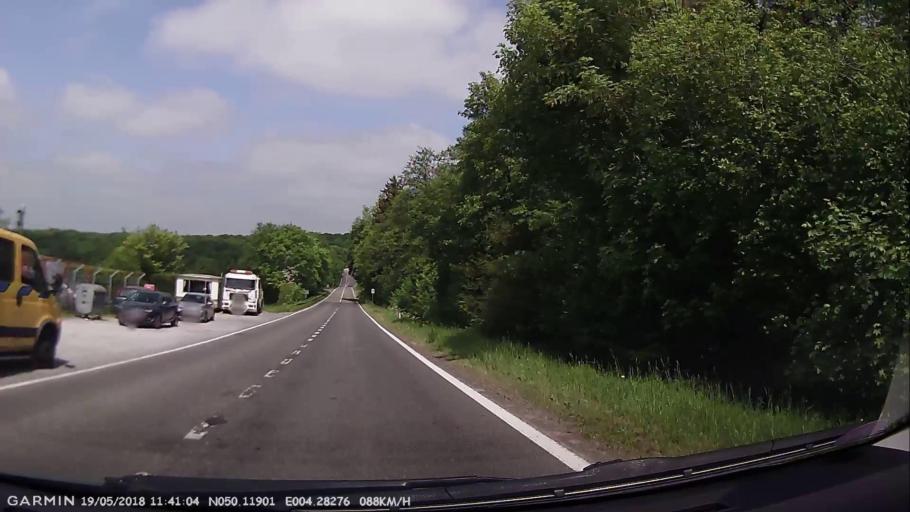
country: BE
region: Wallonia
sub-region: Province du Hainaut
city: Froidchapelle
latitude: 50.1193
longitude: 4.2826
